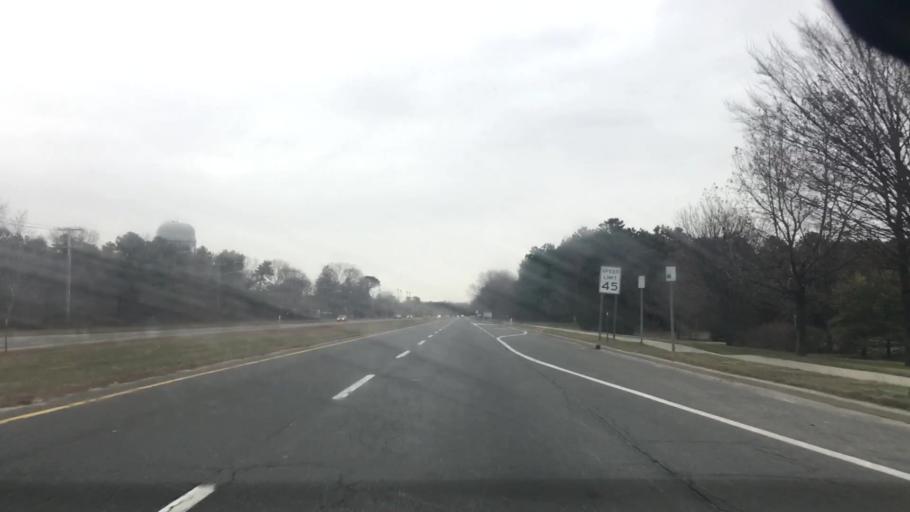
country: US
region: New York
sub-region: Suffolk County
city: North Bellport
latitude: 40.8124
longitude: -72.9518
